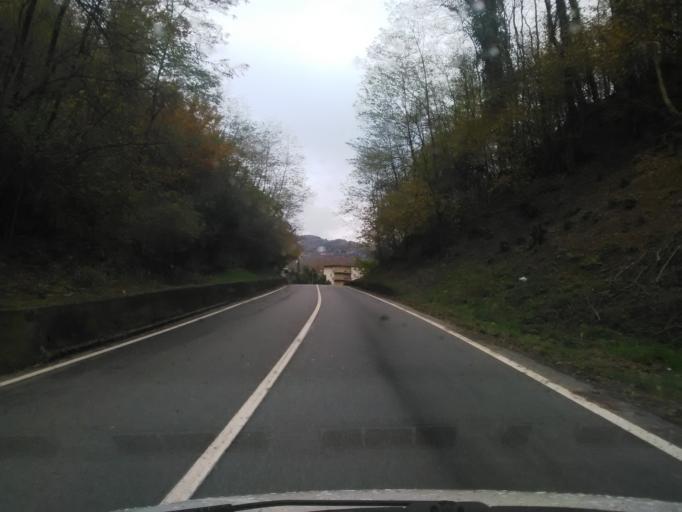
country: IT
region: Piedmont
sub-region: Provincia di Vercelli
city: Borgosesia
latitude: 45.7178
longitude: 8.3010
